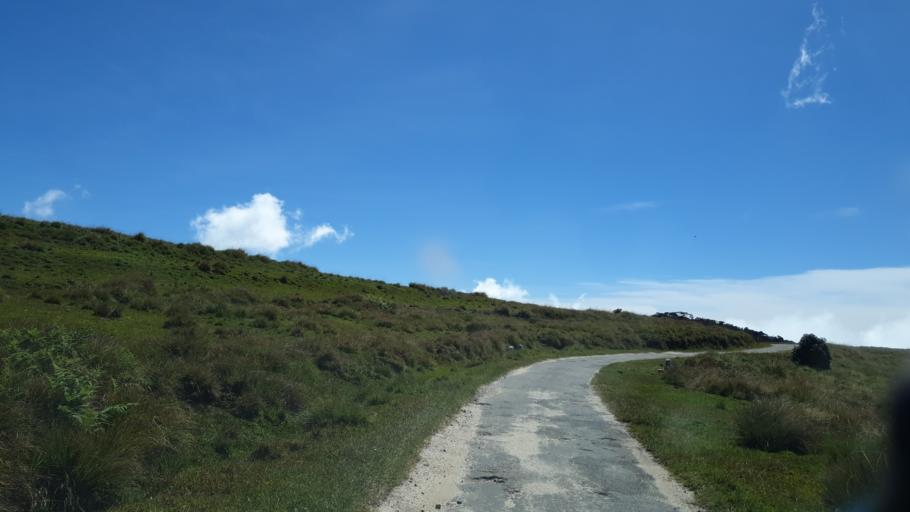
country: LK
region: Uva
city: Haputale
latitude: 6.7983
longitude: 80.8166
